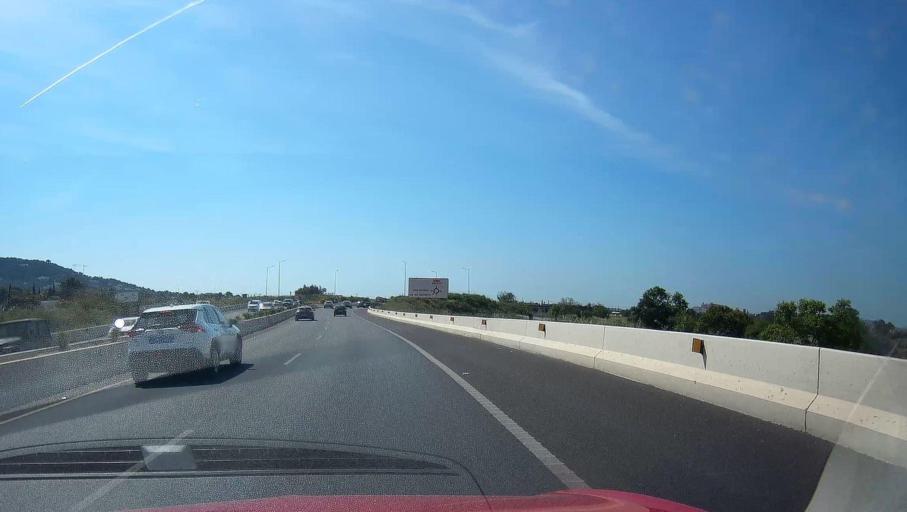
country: ES
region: Balearic Islands
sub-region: Illes Balears
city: Ibiza
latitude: 38.9438
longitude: 1.4435
